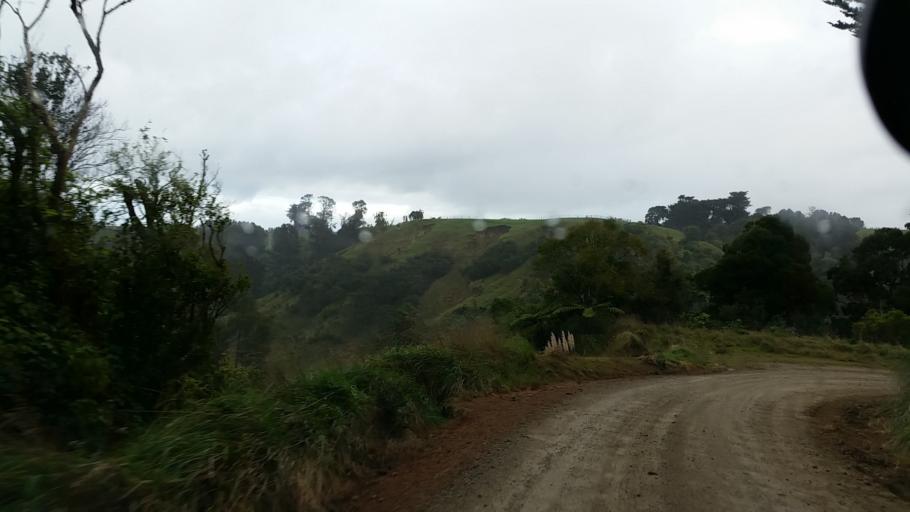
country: NZ
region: Taranaki
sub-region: South Taranaki District
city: Patea
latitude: -39.7626
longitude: 174.7077
